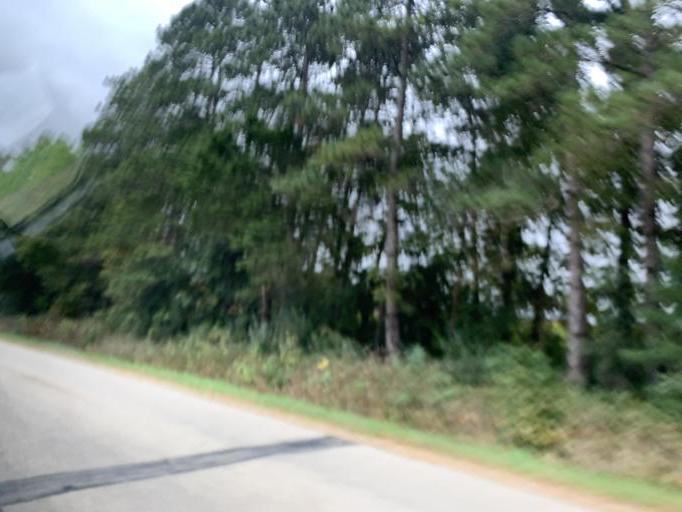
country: US
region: Wisconsin
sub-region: Sauk County
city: Prairie du Sac
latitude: 43.2769
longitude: -89.7789
